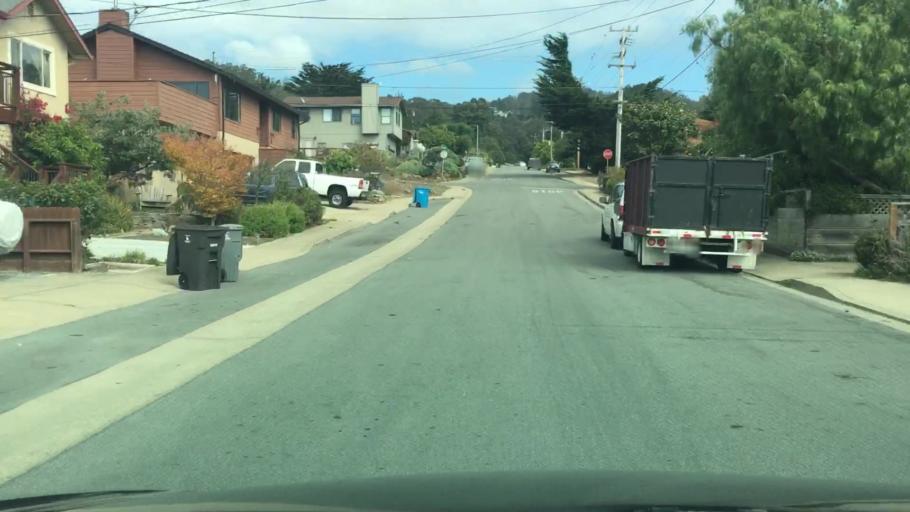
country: US
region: California
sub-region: San Mateo County
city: El Granada
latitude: 37.5071
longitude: -122.4780
